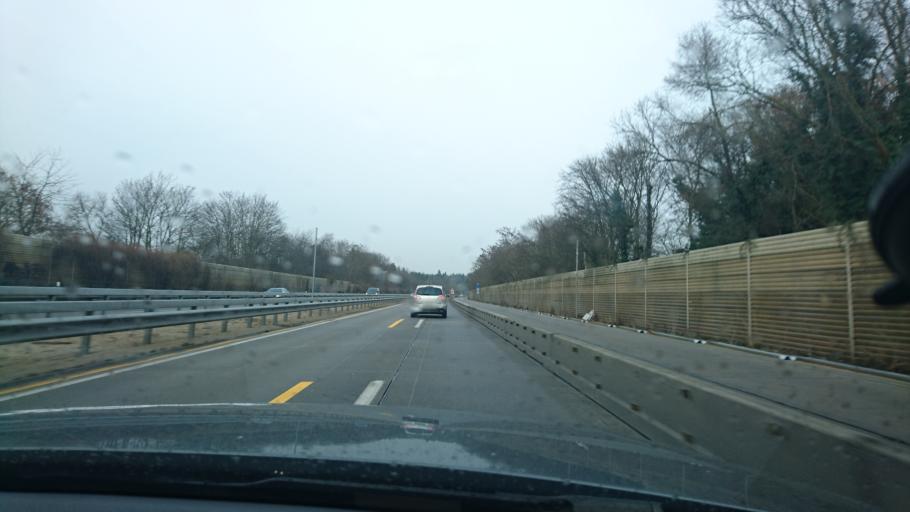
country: DE
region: Schleswig-Holstein
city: Ratekau
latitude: 53.9235
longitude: 10.7260
